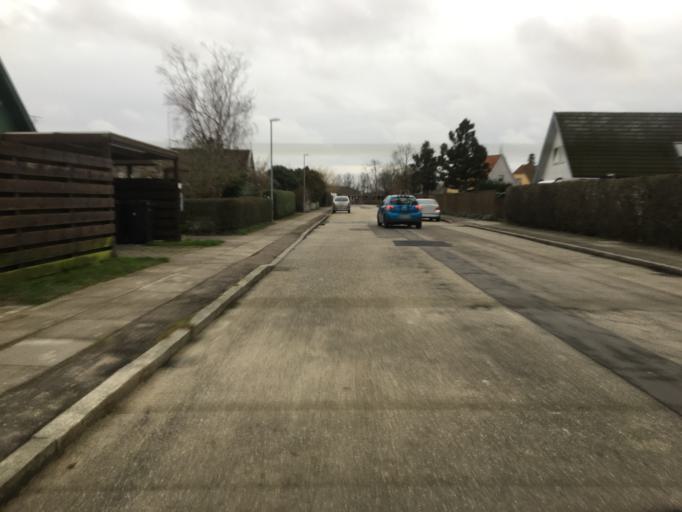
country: DK
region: Capital Region
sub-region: Tarnby Kommune
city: Tarnby
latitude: 55.6201
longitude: 12.6211
